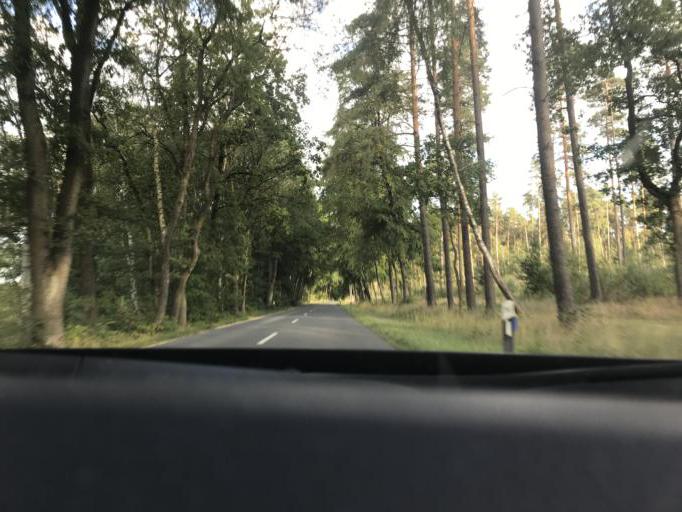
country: DE
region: Lower Saxony
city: Suderburg
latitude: 52.8895
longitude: 10.4946
